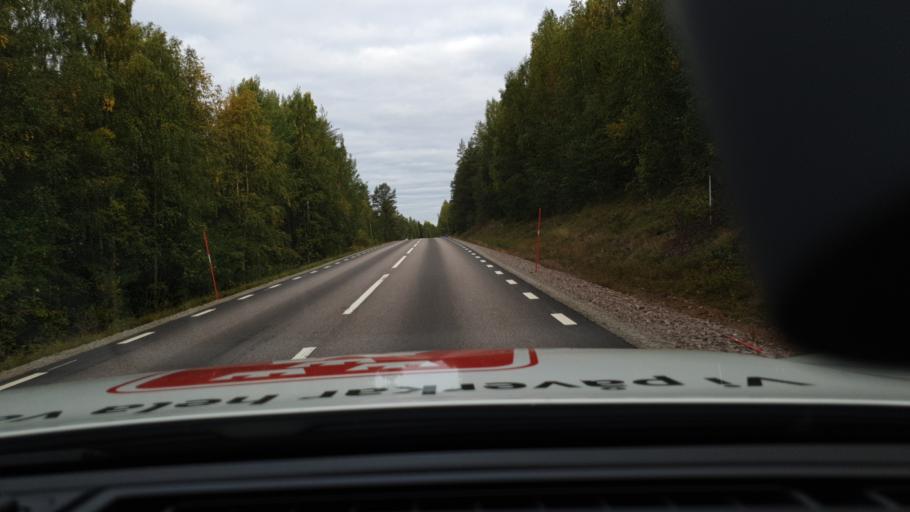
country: SE
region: Norrbotten
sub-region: Overkalix Kommun
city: OEverkalix
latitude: 66.4857
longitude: 22.7826
